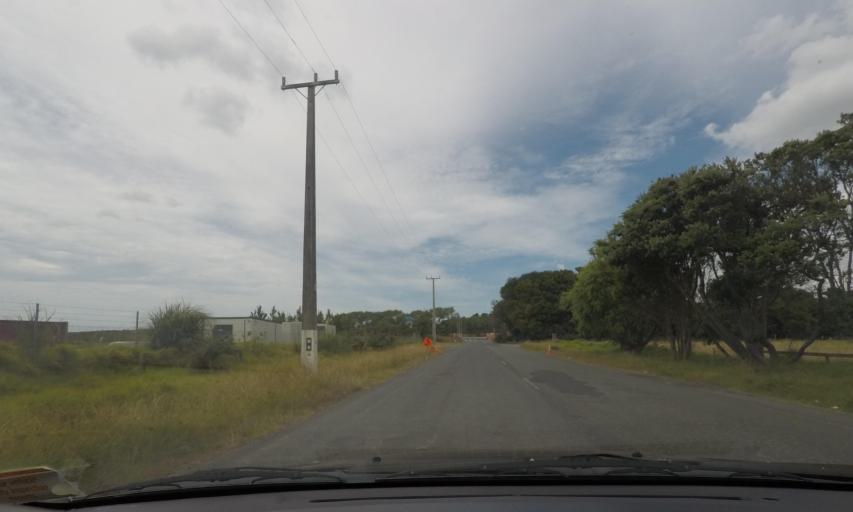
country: NZ
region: Auckland
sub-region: Auckland
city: Mangere
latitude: -36.9944
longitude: 174.7838
